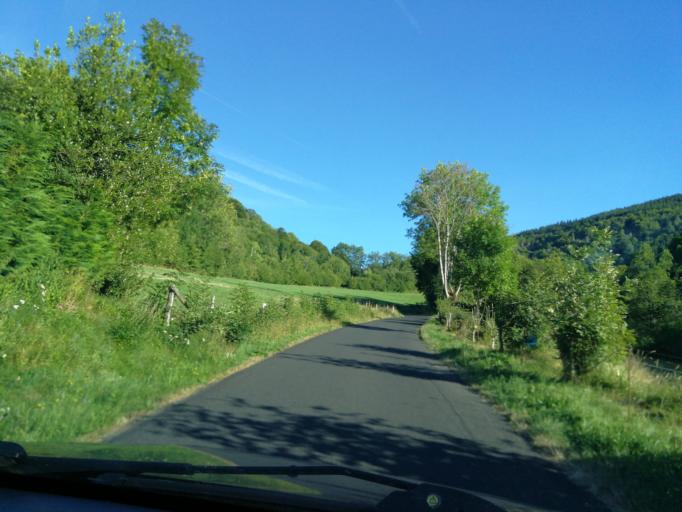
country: FR
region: Auvergne
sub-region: Departement du Cantal
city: Vic-sur-Cere
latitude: 45.0842
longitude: 2.5668
